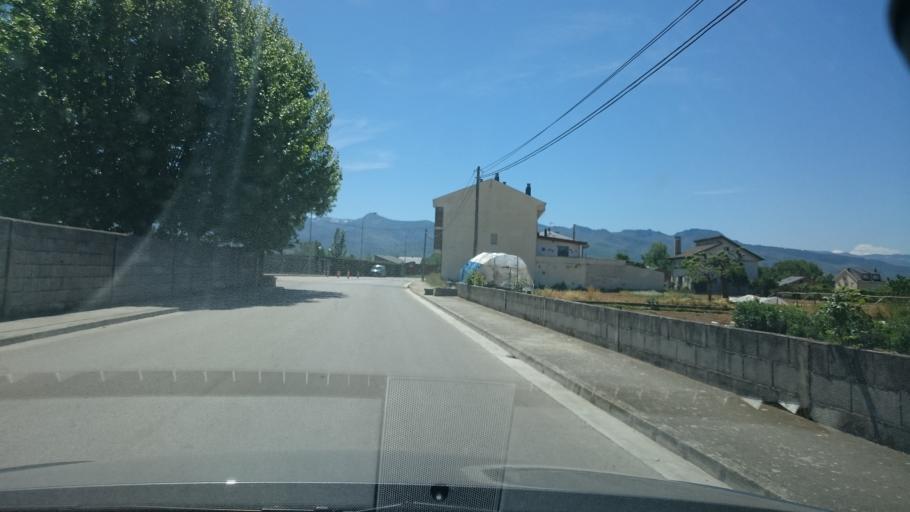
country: ES
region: Castille and Leon
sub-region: Provincia de Leon
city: Camponaraya
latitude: 42.5750
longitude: -6.6630
